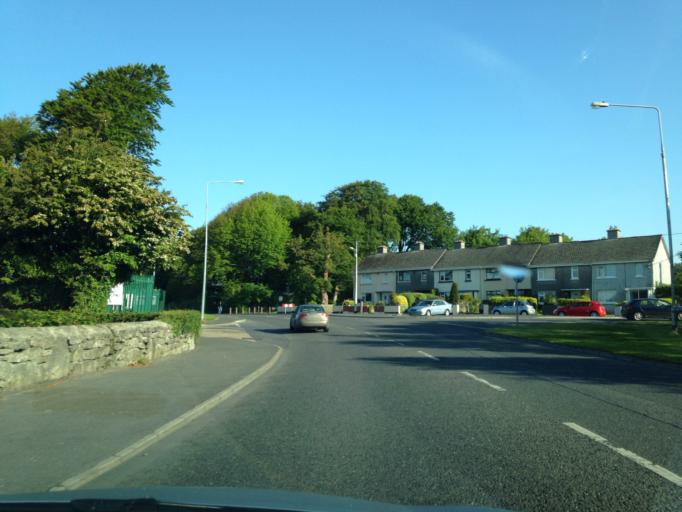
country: IE
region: Connaught
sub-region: County Galway
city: Gaillimh
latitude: 53.2837
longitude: -9.0181
